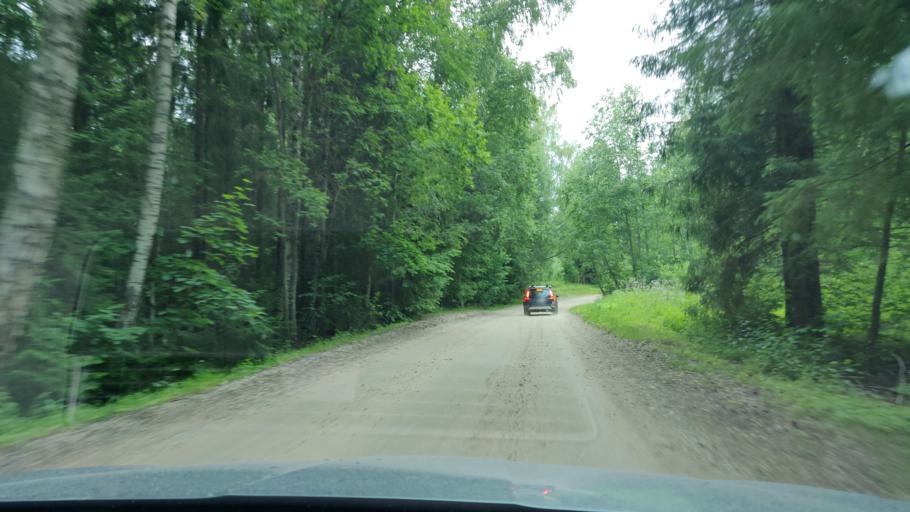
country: EE
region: Vorumaa
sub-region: Antsla vald
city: Vana-Antsla
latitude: 58.0309
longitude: 26.5500
